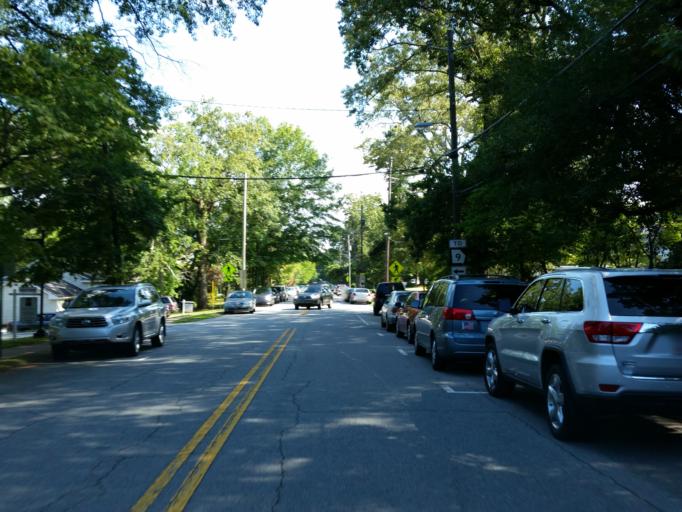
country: US
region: Georgia
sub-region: Fulton County
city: Roswell
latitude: 34.0220
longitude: -84.3633
